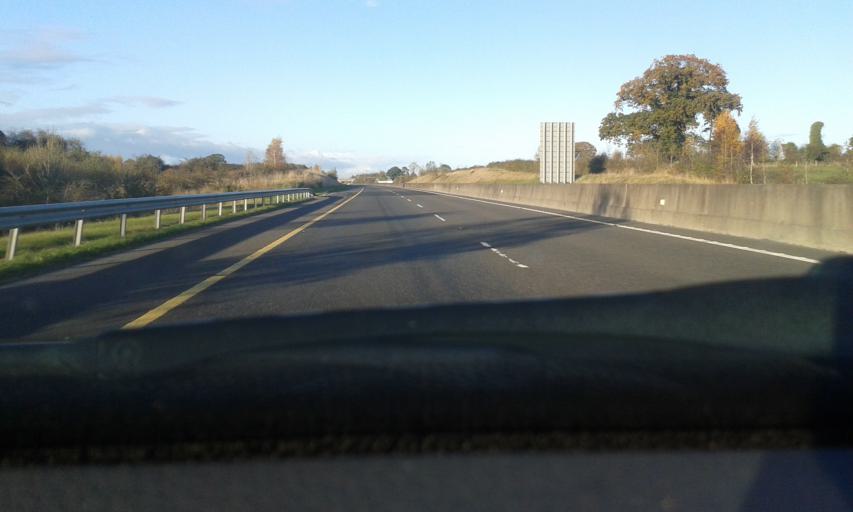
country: IE
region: Leinster
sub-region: Laois
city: Rathdowney
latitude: 52.7426
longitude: -7.5763
